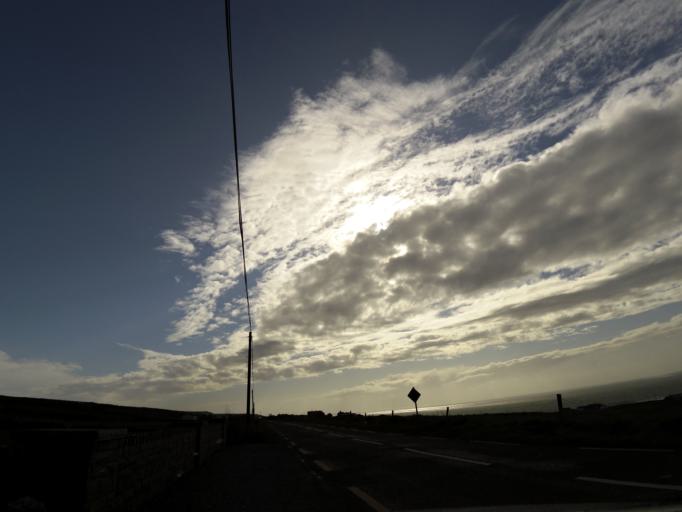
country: IE
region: Connaught
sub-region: County Galway
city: Bearna
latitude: 52.9996
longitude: -9.3832
